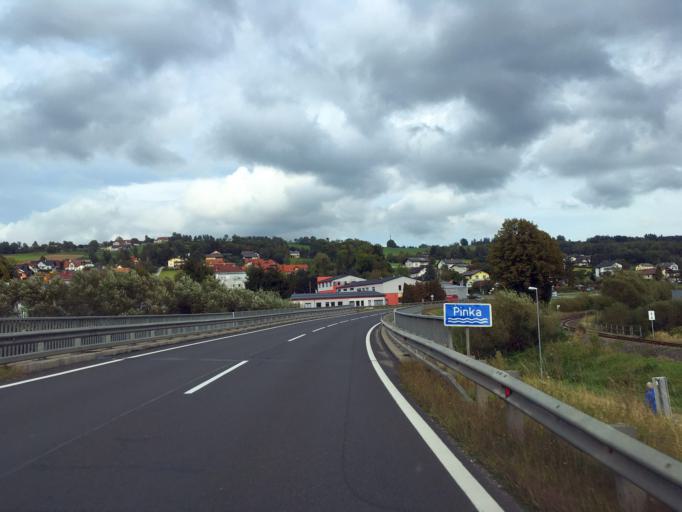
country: AT
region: Styria
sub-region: Politischer Bezirk Hartberg-Fuerstenfeld
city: Pinggau
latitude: 47.4381
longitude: 16.0680
